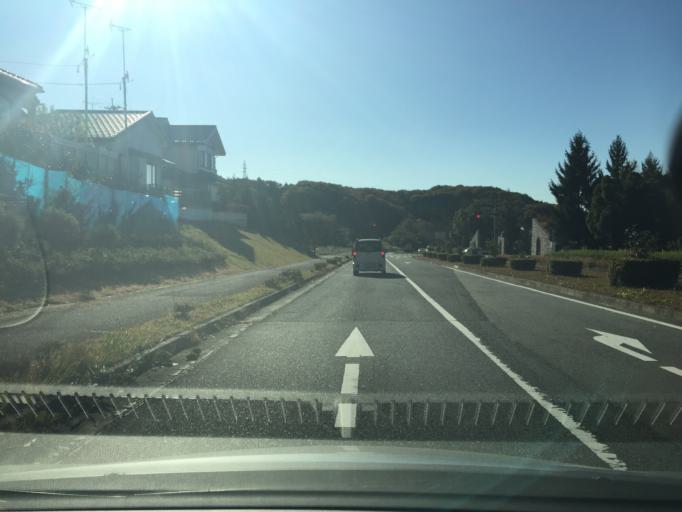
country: JP
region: Fukushima
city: Iwaki
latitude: 37.0168
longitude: 140.8658
